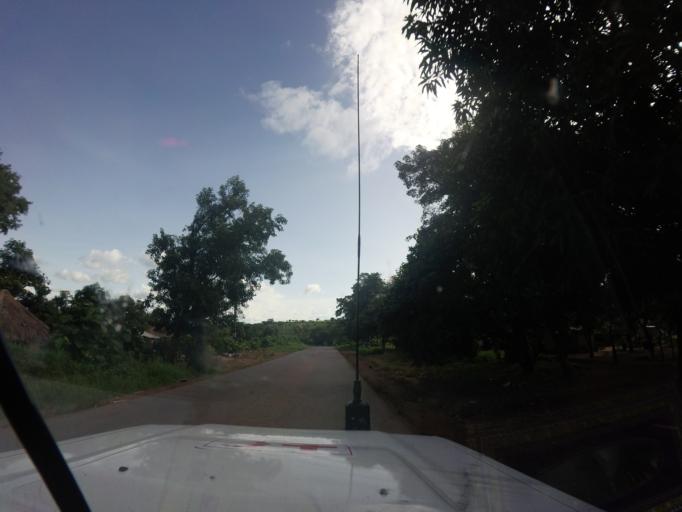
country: GN
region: Kindia
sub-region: Kindia
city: Kindia
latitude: 10.1231
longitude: -12.5449
